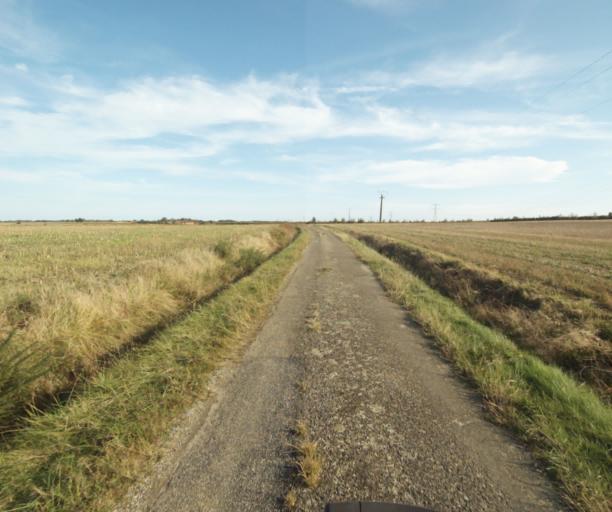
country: FR
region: Midi-Pyrenees
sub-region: Departement du Tarn-et-Garonne
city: Finhan
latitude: 43.9077
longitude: 1.1121
